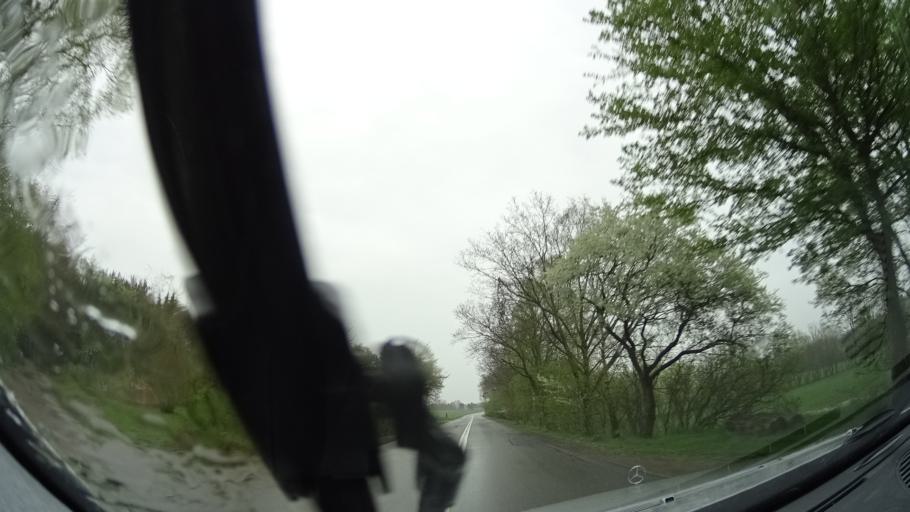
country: DK
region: Zealand
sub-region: Odsherred Kommune
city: Asnaes
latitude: 55.8519
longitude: 11.5446
